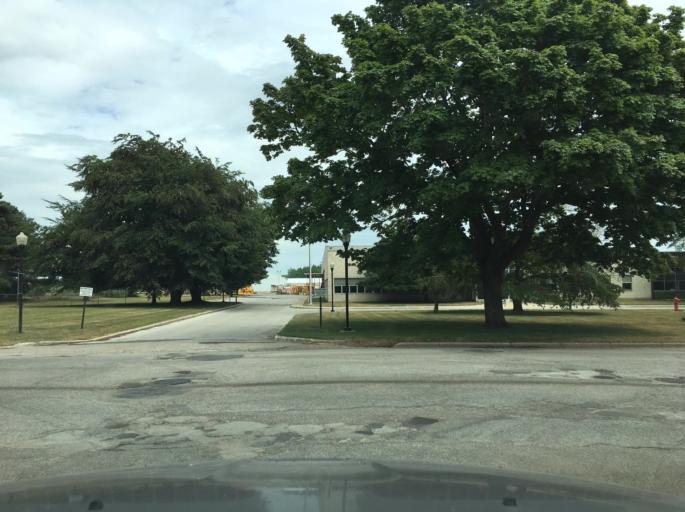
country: US
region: Michigan
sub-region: Mason County
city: Ludington
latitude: 43.9543
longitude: -86.4295
